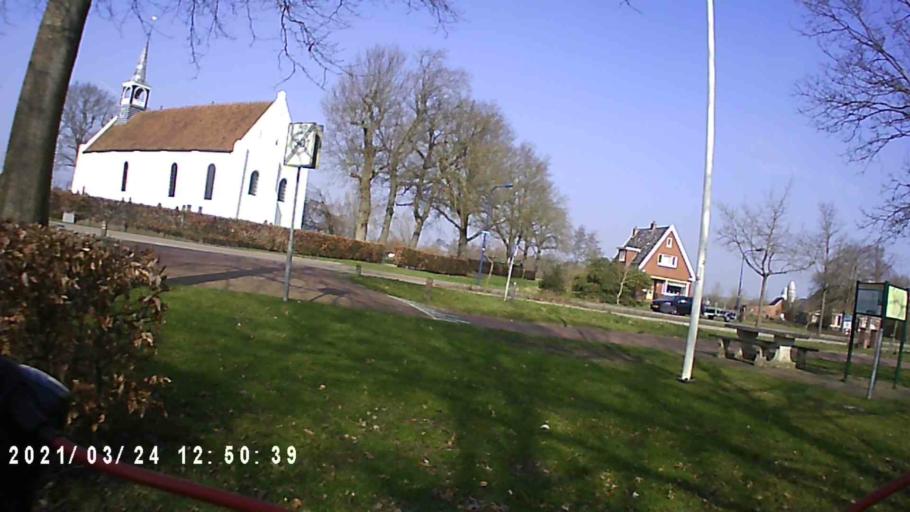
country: NL
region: Groningen
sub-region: Gemeente Leek
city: Leek
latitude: 53.1624
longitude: 6.3292
